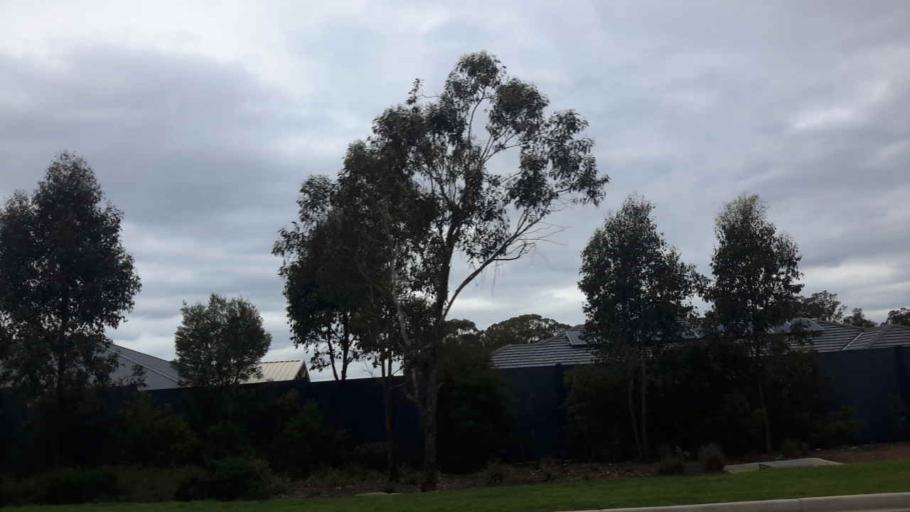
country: AU
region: New South Wales
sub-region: Penrith Municipality
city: Werrington Downs
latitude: -33.7247
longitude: 150.7216
